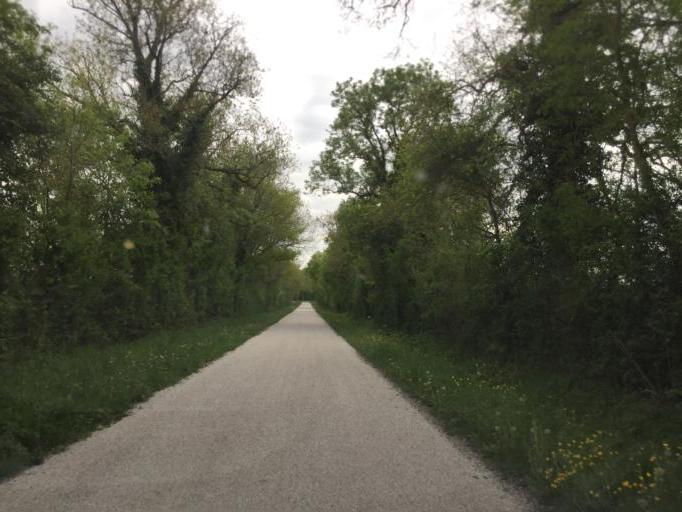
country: FR
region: Rhone-Alpes
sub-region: Departement de l'Ain
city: Tramoyes
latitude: 45.9024
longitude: 4.9783
